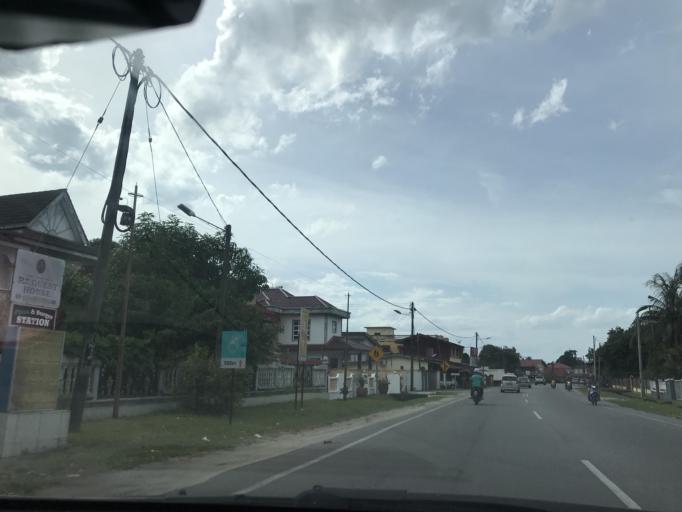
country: MY
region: Kelantan
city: Kota Bharu
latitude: 6.0980
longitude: 102.2304
